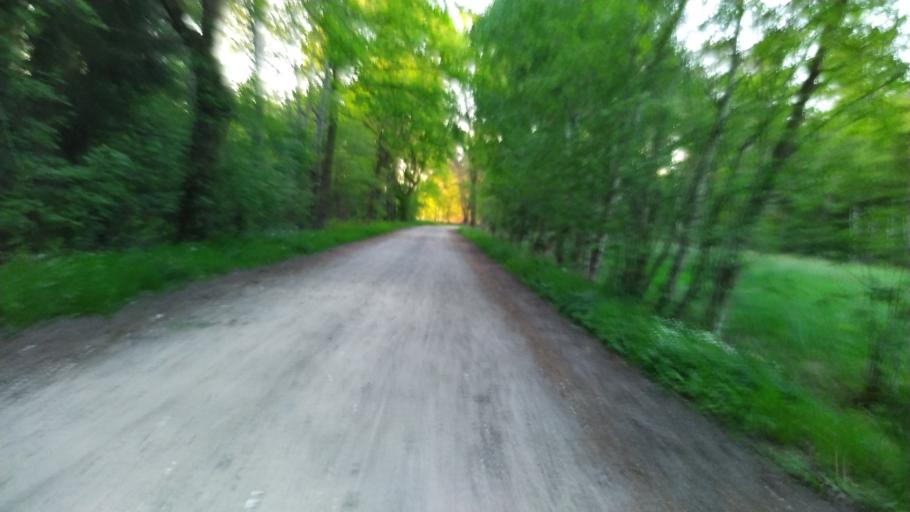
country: DE
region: Lower Saxony
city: Bargstedt
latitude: 53.4871
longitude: 9.4396
